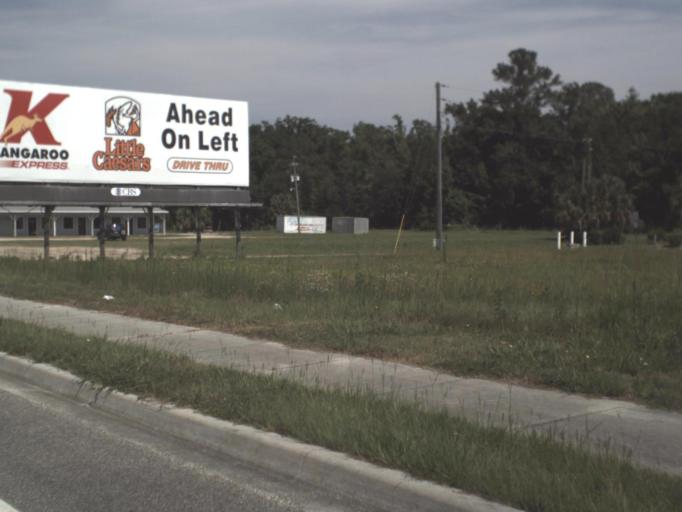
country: US
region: Florida
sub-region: Putnam County
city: East Palatka
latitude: 29.7145
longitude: -81.5043
